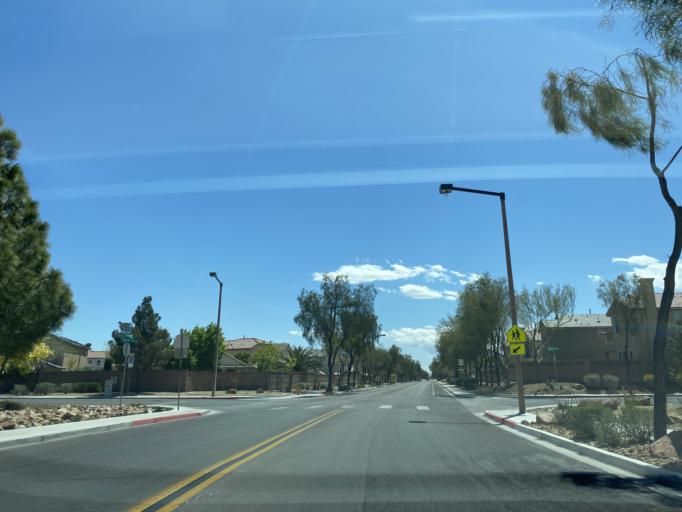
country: US
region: Nevada
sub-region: Clark County
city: North Las Vegas
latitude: 36.3172
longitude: -115.2116
